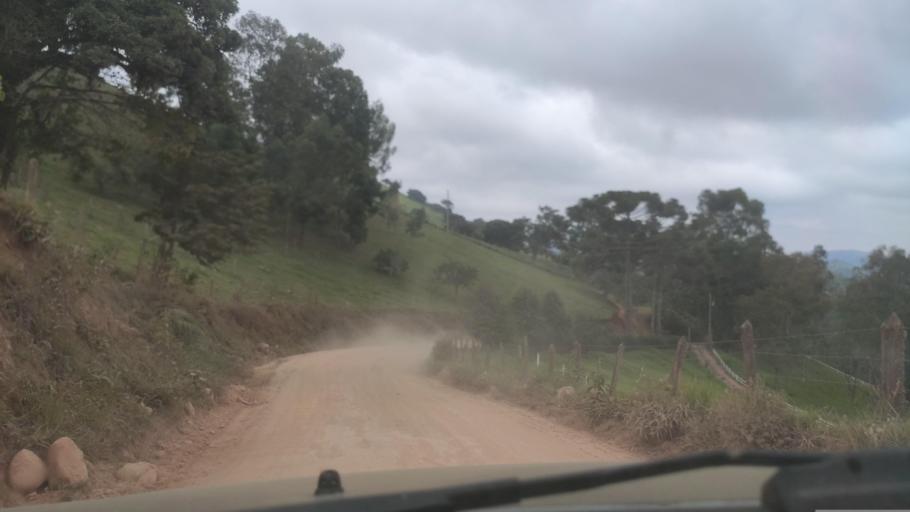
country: BR
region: Minas Gerais
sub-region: Paraisopolis
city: Paraisopolis
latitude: -22.6615
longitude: -45.8789
